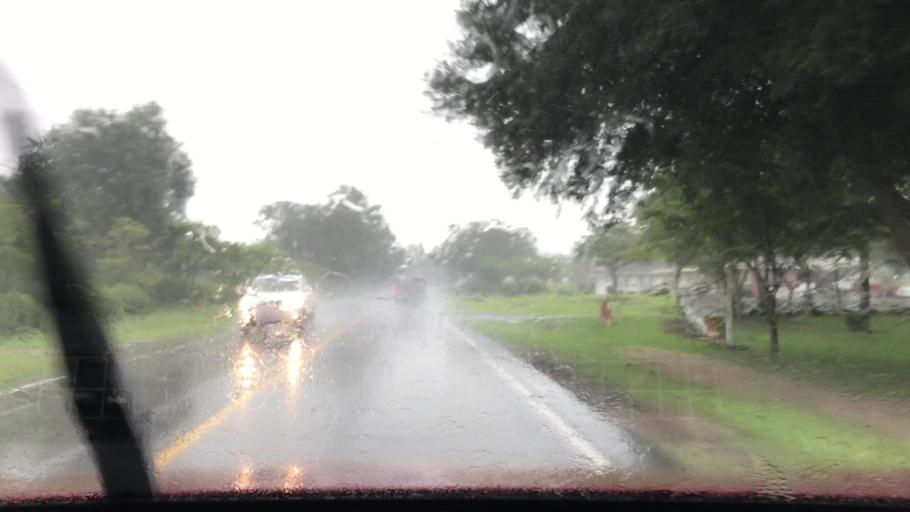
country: US
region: South Carolina
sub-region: Horry County
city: Red Hill
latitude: 33.9021
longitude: -78.8886
